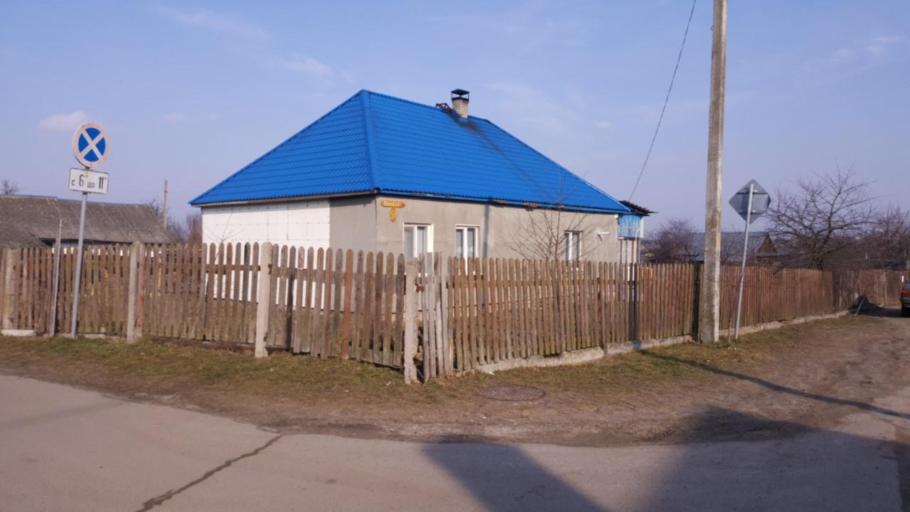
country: BY
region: Brest
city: Kamyanyets
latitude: 52.4053
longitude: 23.8222
